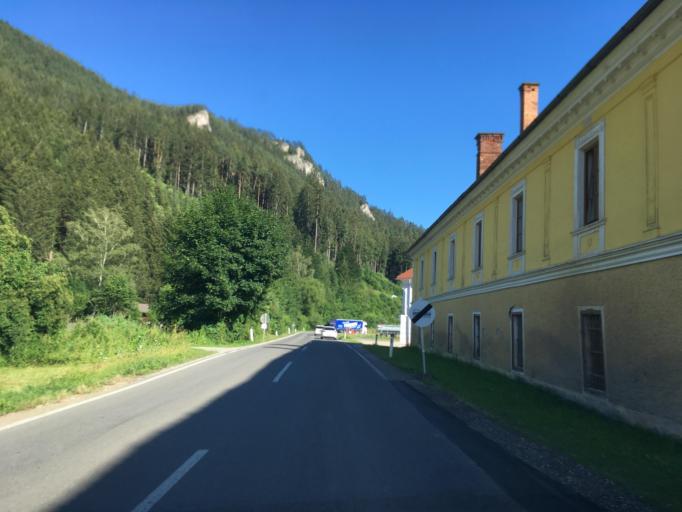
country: AT
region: Styria
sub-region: Politischer Bezirk Leoben
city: Trofaiach
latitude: 47.4113
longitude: 15.0258
